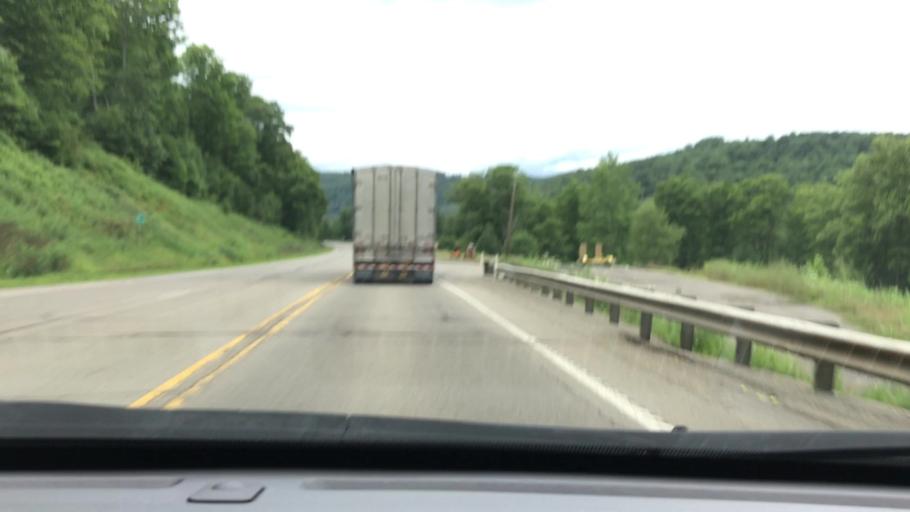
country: US
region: Pennsylvania
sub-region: McKean County
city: Kane
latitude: 41.7608
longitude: -78.7019
